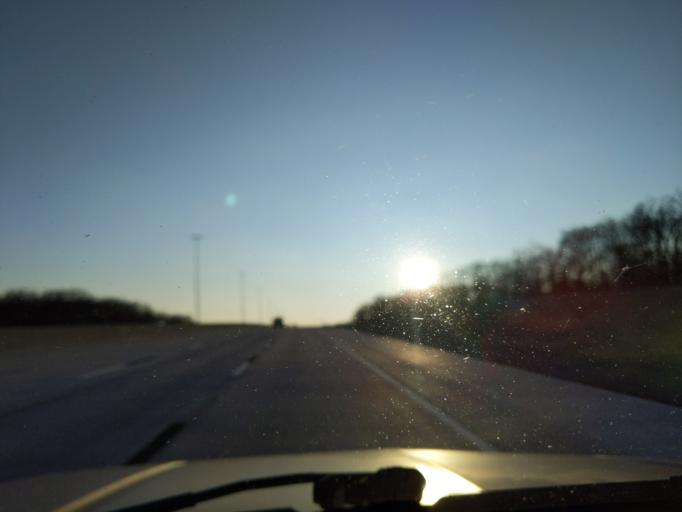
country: US
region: Oklahoma
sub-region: Creek County
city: Kellyville
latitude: 35.9338
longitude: -96.2680
